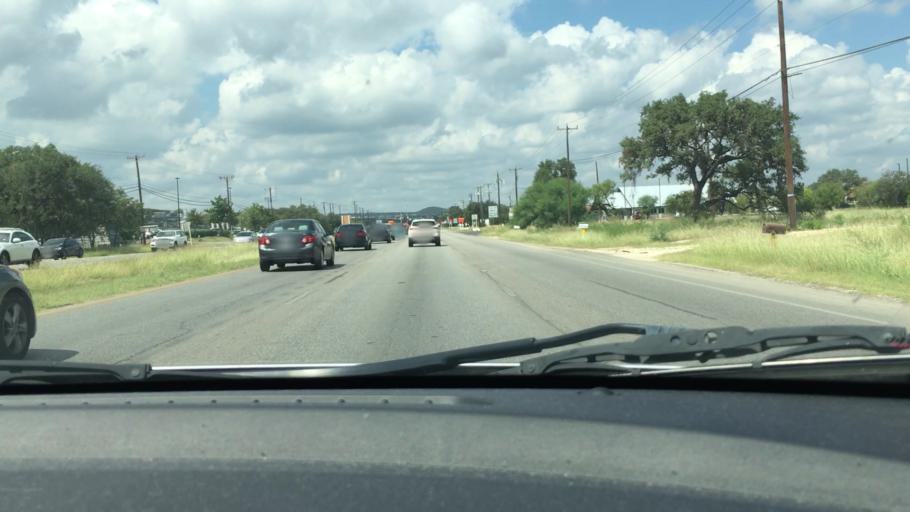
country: US
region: Texas
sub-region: Bexar County
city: Helotes
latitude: 29.5596
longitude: -98.6761
